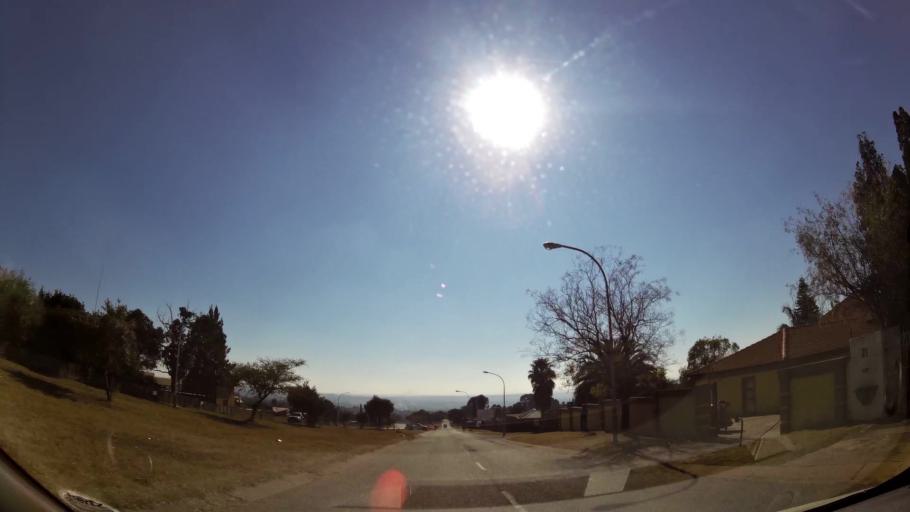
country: ZA
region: Mpumalanga
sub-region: Nkangala District Municipality
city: Witbank
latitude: -25.8688
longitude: 29.2410
